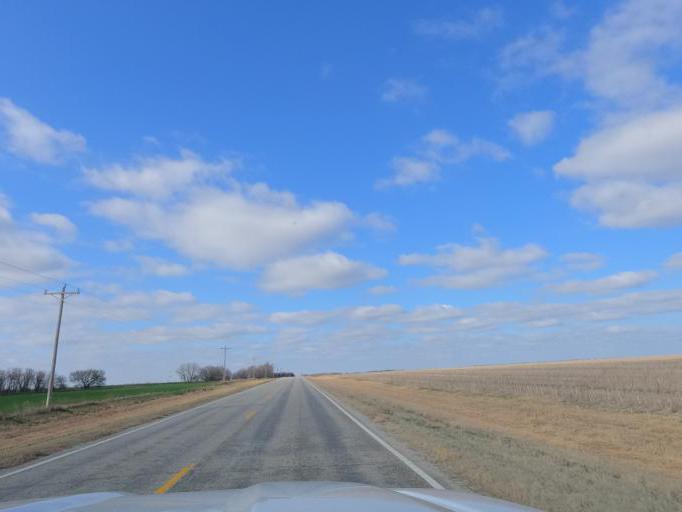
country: US
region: Kansas
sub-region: McPherson County
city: Inman
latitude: 38.1908
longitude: -97.8486
